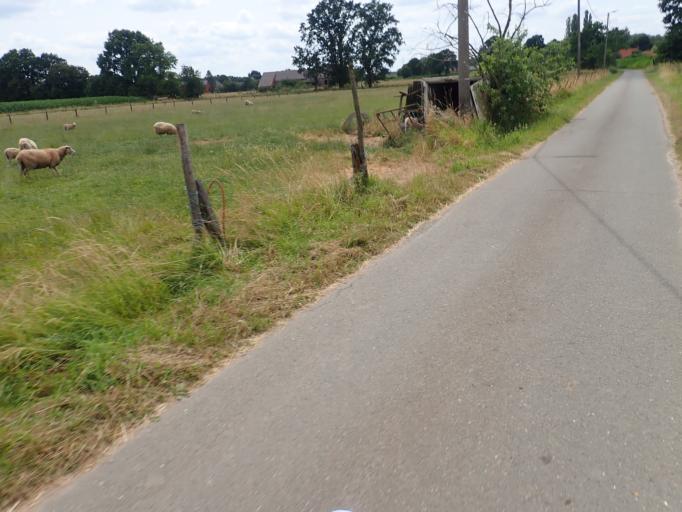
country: BE
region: Flanders
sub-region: Provincie Antwerpen
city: Putte
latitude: 51.0363
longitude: 4.6281
